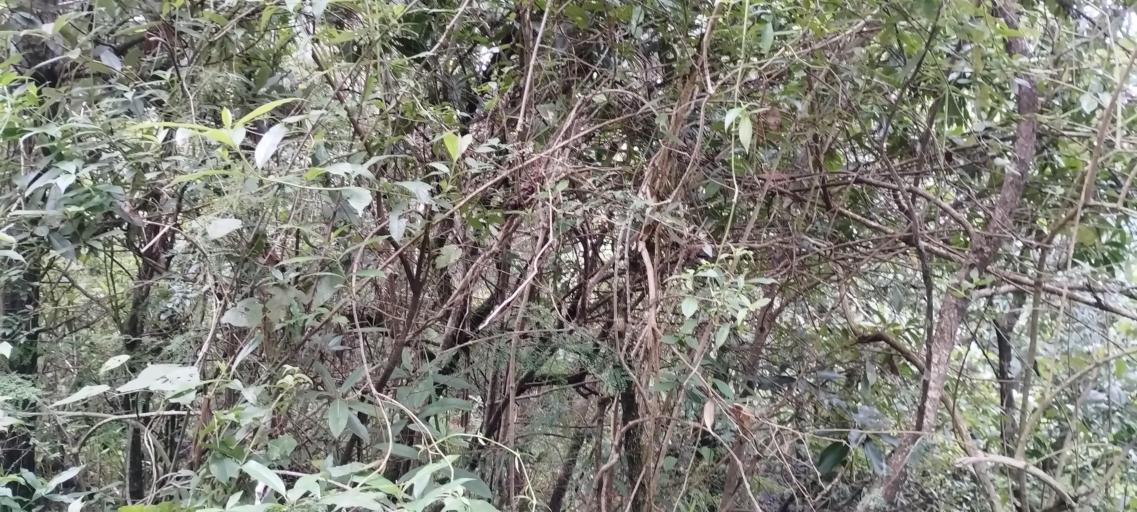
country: NP
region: Central Region
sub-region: Bagmati Zone
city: Kathmandu
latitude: 27.7878
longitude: 85.3786
